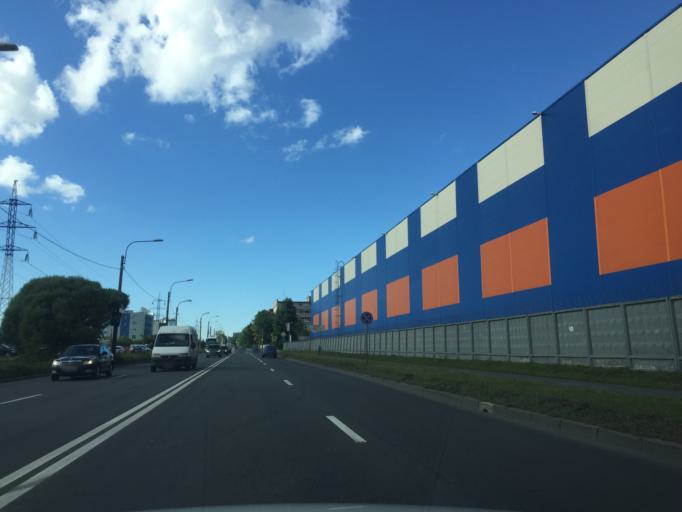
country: RU
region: St.-Petersburg
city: Dachnoye
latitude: 59.8387
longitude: 30.3020
